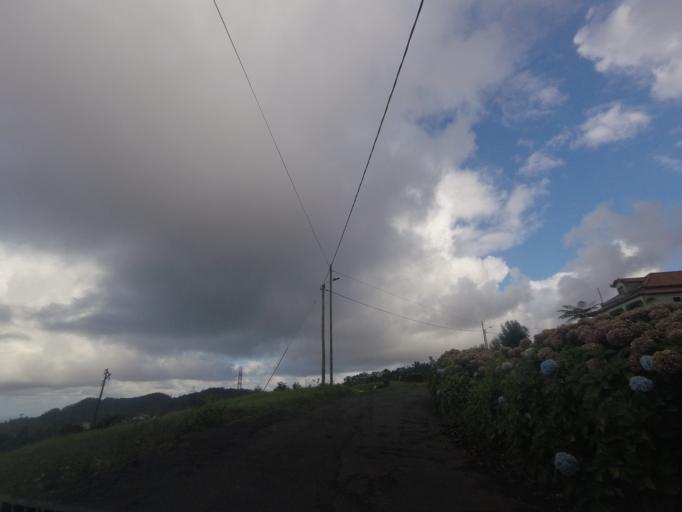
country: PT
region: Madeira
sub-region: Santana
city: Santana
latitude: 32.7999
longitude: -16.8875
